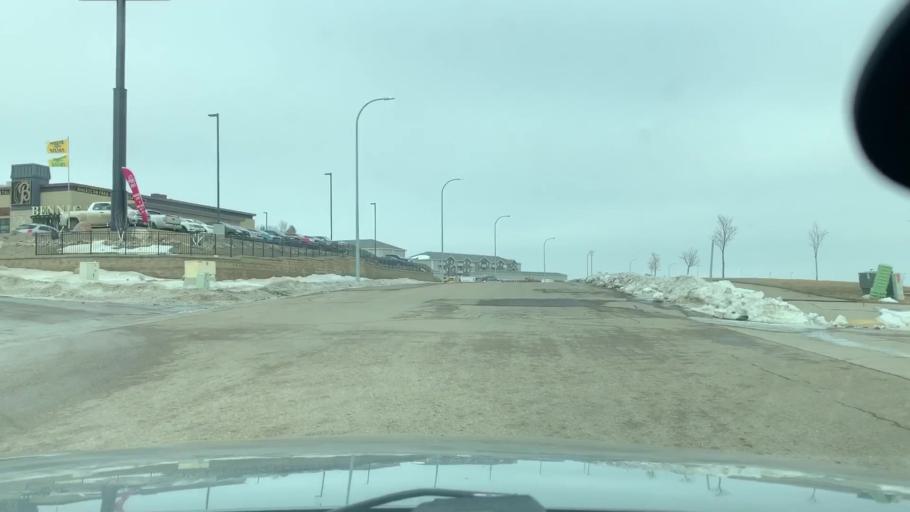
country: US
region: North Dakota
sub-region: Morton County
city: Mandan
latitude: 46.8501
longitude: -100.9096
